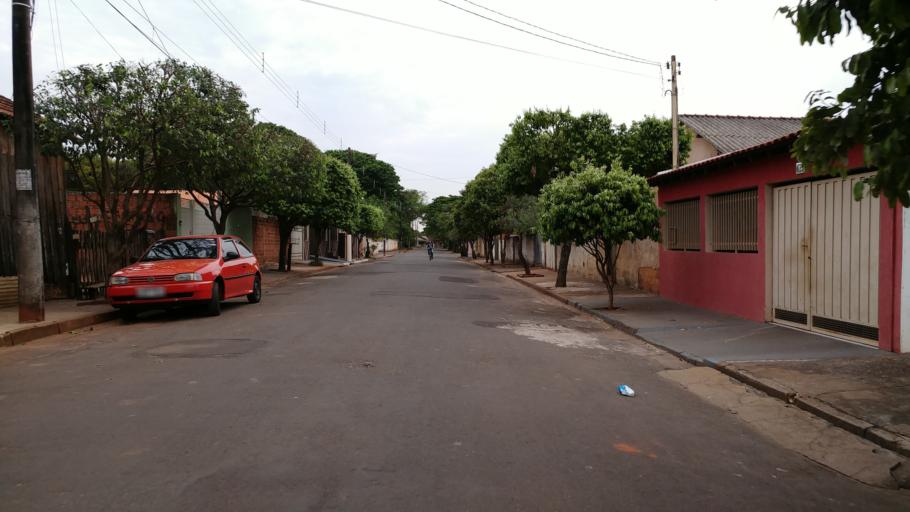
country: BR
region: Sao Paulo
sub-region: Paraguacu Paulista
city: Paraguacu Paulista
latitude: -22.4135
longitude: -50.5700
